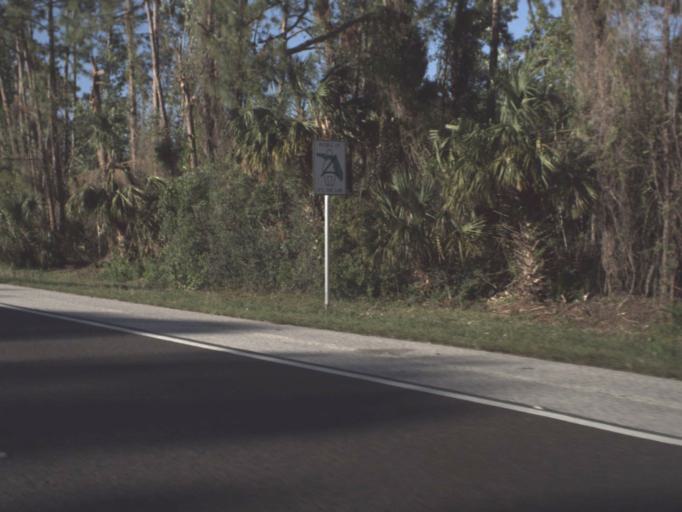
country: US
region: Florida
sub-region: Flagler County
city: Flagler Beach
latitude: 29.4698
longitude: -81.1813
